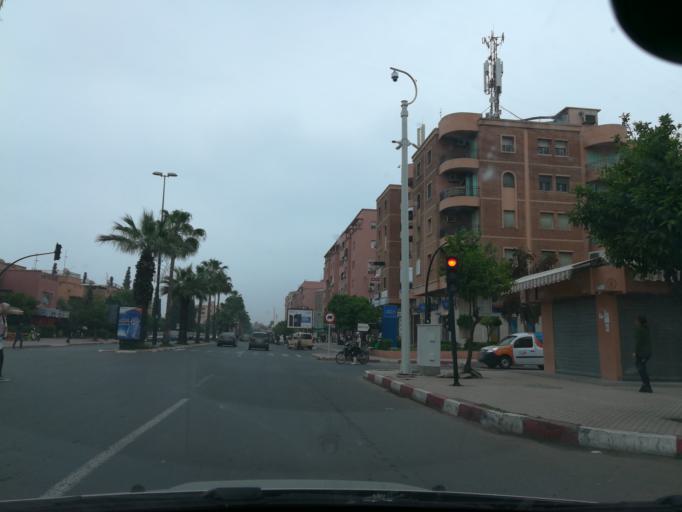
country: MA
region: Marrakech-Tensift-Al Haouz
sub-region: Marrakech
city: Marrakesh
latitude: 31.6557
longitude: -8.0037
